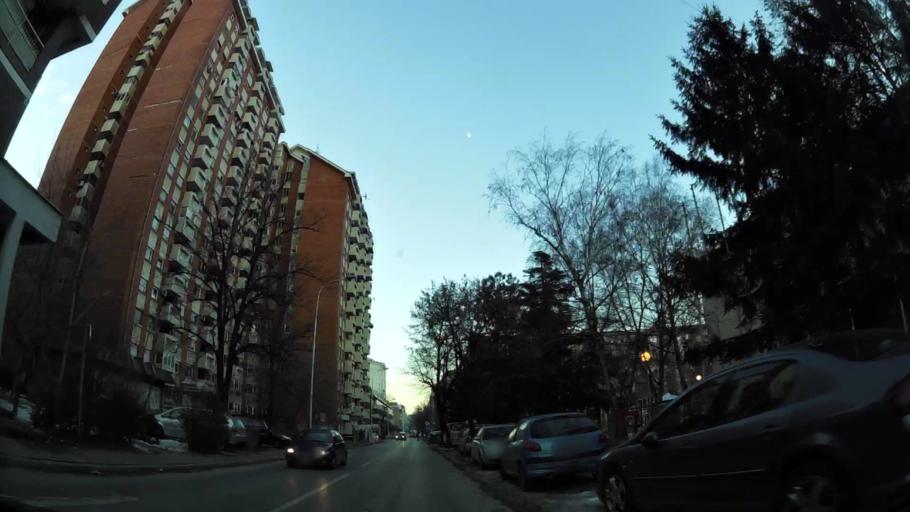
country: MK
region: Karpos
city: Skopje
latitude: 41.9928
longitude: 21.4175
